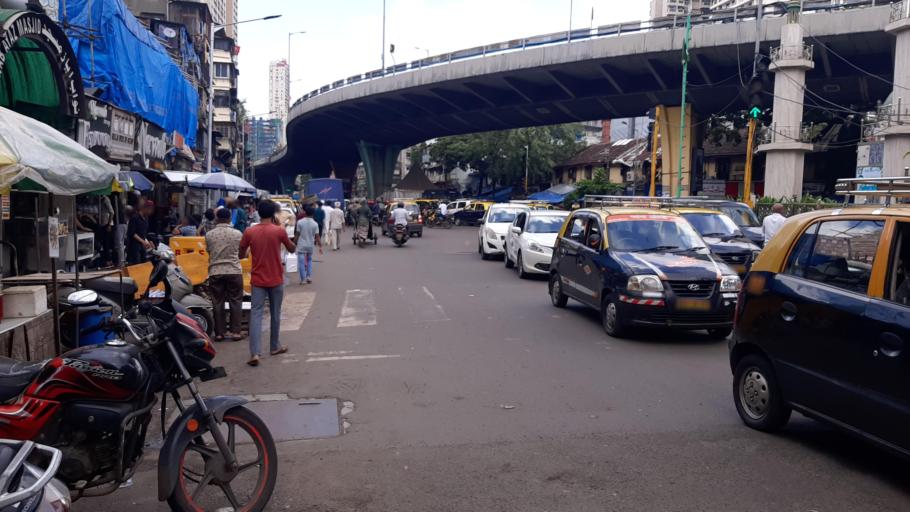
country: IN
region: Maharashtra
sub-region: Mumbai Suburban
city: Mumbai
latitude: 18.9568
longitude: 72.8320
